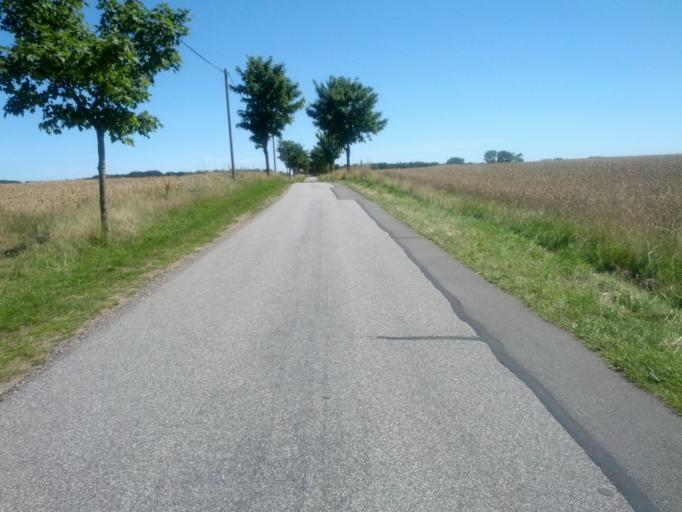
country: DE
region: Mecklenburg-Vorpommern
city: Bastorf
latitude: 54.1195
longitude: 11.6590
